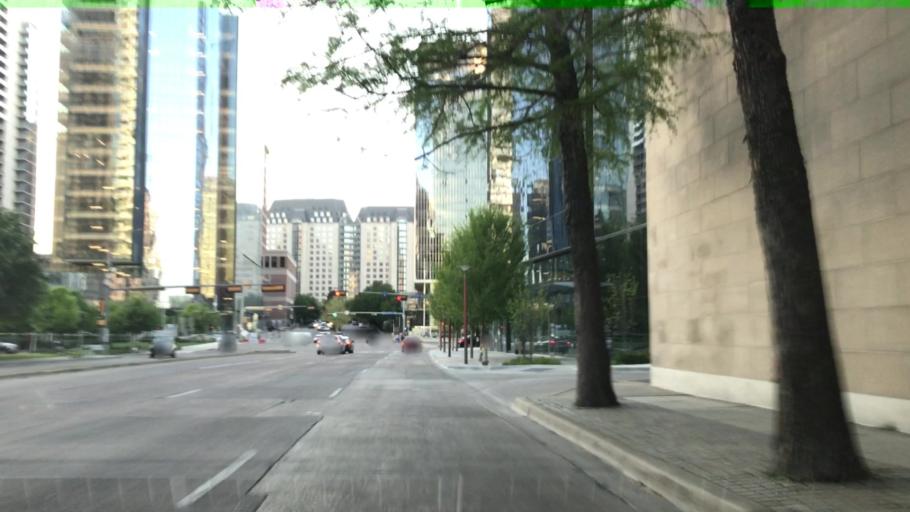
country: US
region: Texas
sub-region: Dallas County
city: Dallas
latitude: 32.7897
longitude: -96.7993
